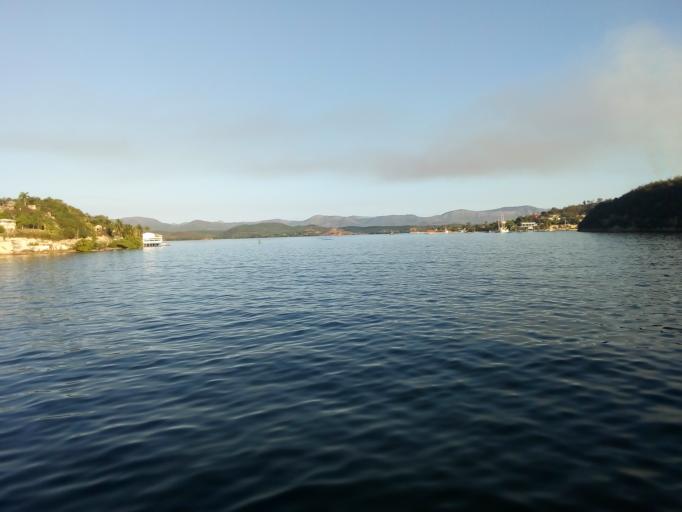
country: CU
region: Santiago de Cuba
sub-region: Municipio de Santiago de Cuba
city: Santiago de Cuba
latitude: 19.9760
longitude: -75.8714
